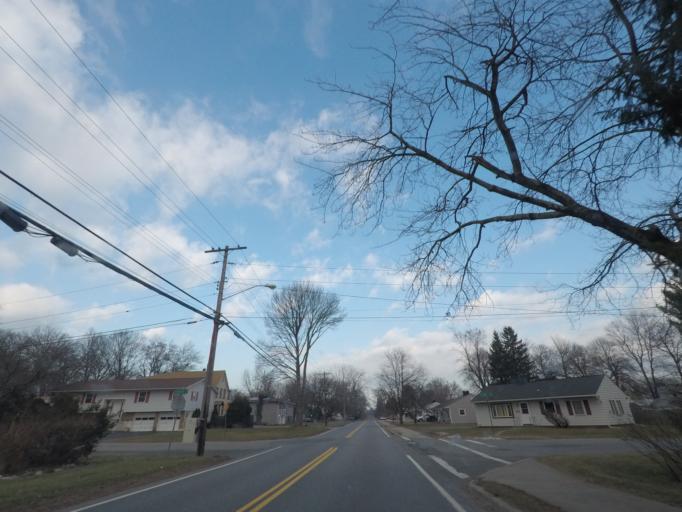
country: US
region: New York
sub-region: Albany County
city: Colonie
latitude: 42.7114
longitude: -73.8371
